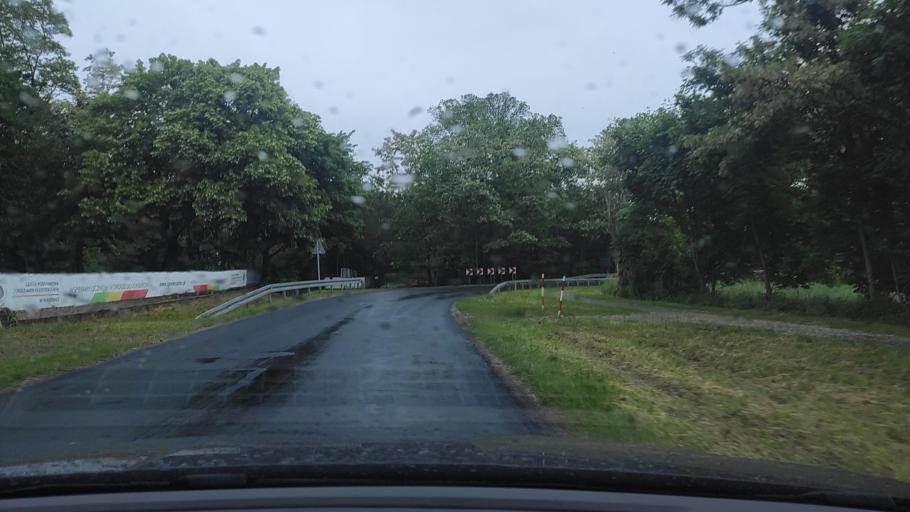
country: PL
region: Greater Poland Voivodeship
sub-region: Powiat poznanski
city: Kobylnica
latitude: 52.4879
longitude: 17.0918
